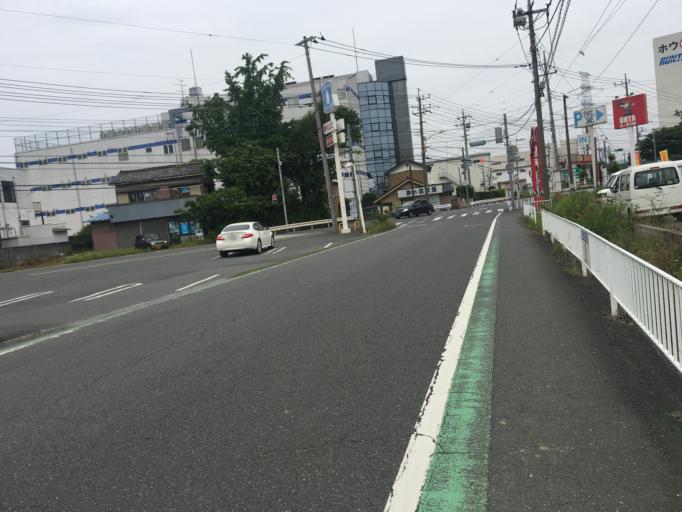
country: JP
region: Saitama
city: Sakado
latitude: 35.9938
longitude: 139.4393
